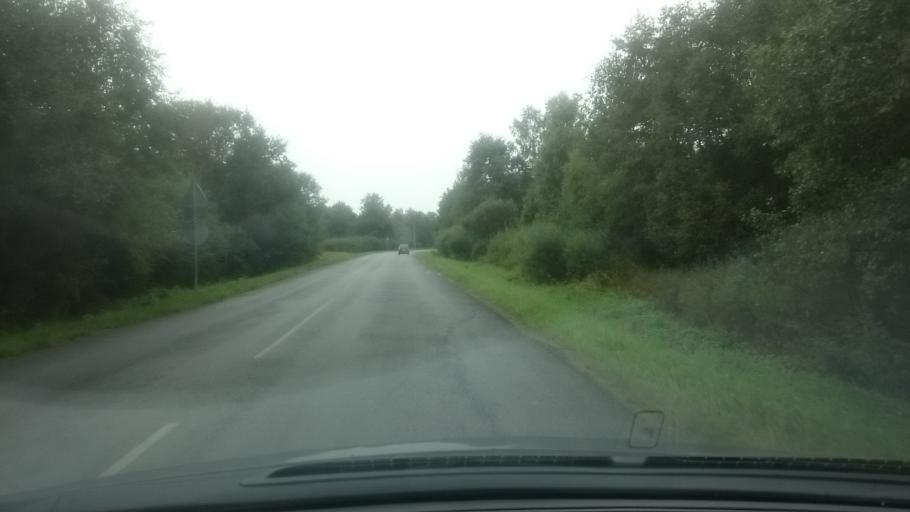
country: EE
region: Harju
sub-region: Raasiku vald
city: Raasiku
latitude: 59.4503
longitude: 25.1994
